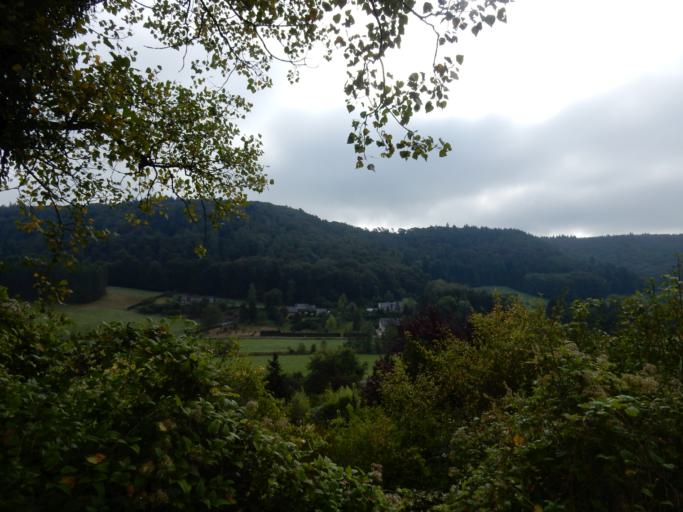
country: LU
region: Luxembourg
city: Rollingen
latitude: 49.7168
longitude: 6.0879
